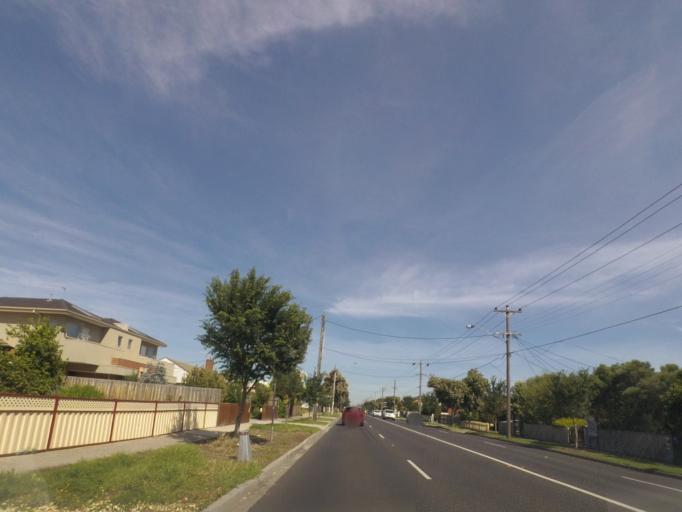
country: AU
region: Victoria
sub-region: Maribyrnong
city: Maidstone
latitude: -37.7855
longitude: 144.8754
